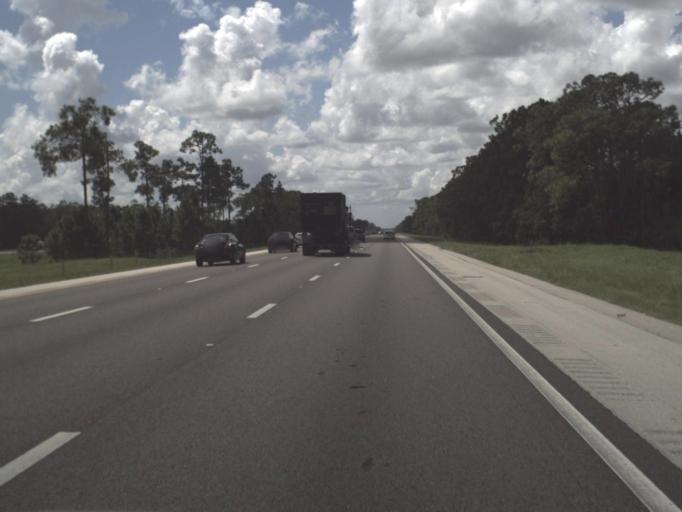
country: US
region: Florida
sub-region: Lee County
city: Estero
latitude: 26.4125
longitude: -81.7735
